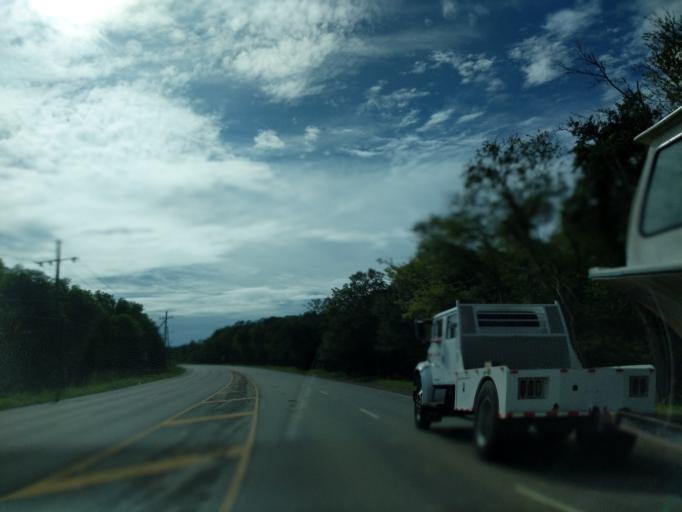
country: US
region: Louisiana
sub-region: Saint Tammany Parish
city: Eden Isle
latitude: 30.0766
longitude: -89.8574
